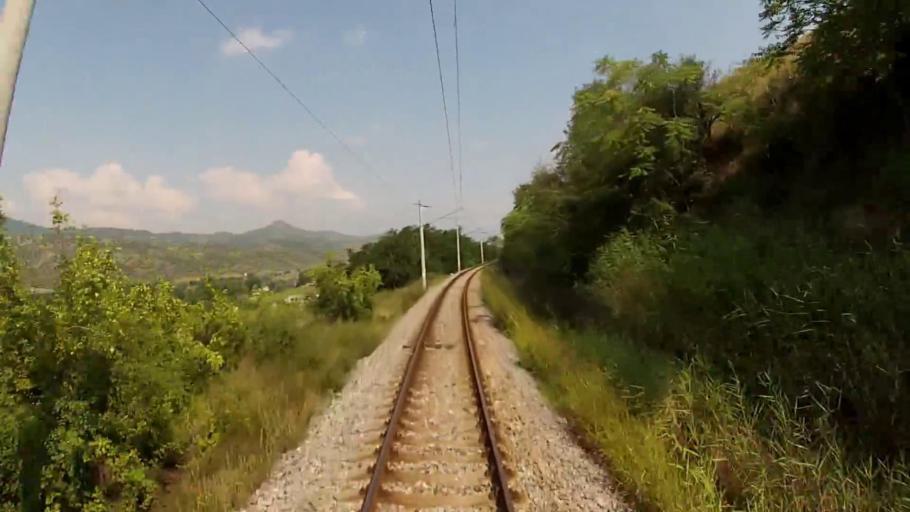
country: BG
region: Blagoevgrad
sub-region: Obshtina Sandanski
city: Sandanski
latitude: 41.5681
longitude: 23.2429
